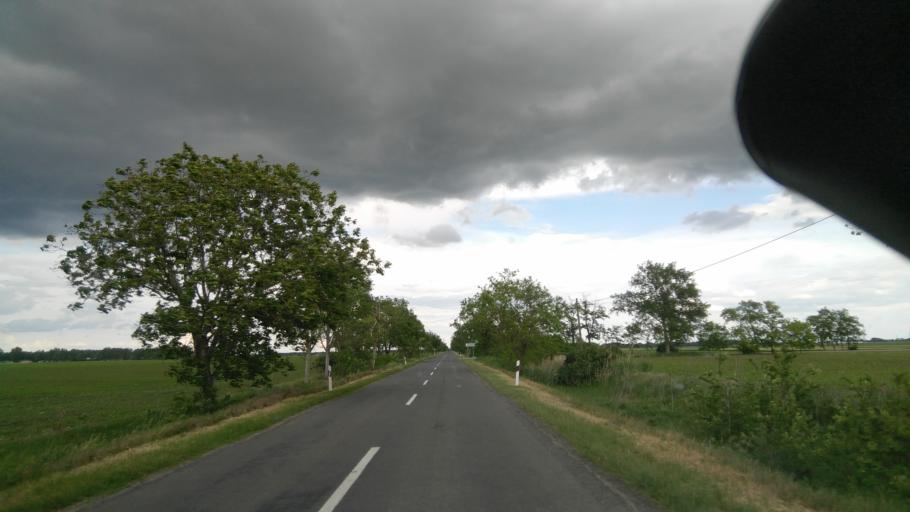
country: HU
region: Bekes
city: Gadoros
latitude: 46.6721
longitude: 20.6274
